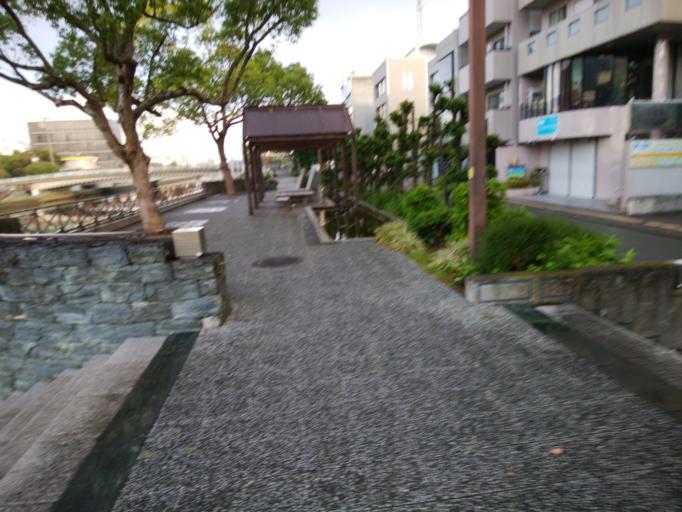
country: JP
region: Tokushima
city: Tokushima-shi
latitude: 34.0708
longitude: 134.5494
